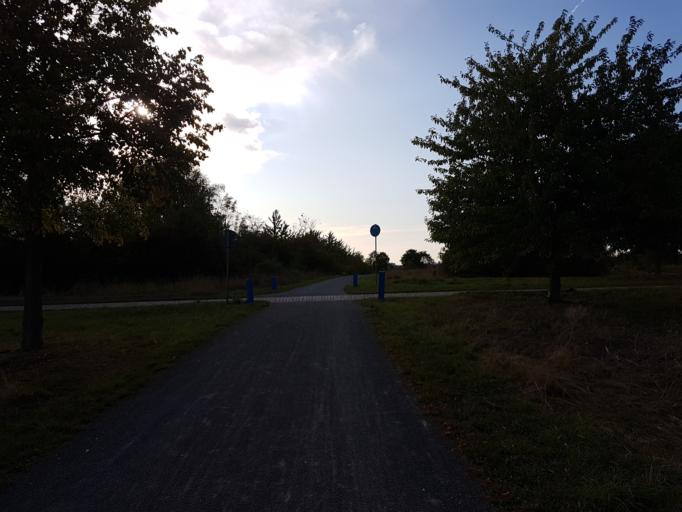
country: DE
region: Lower Saxony
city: Laatzen
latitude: 52.3490
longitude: 9.8554
